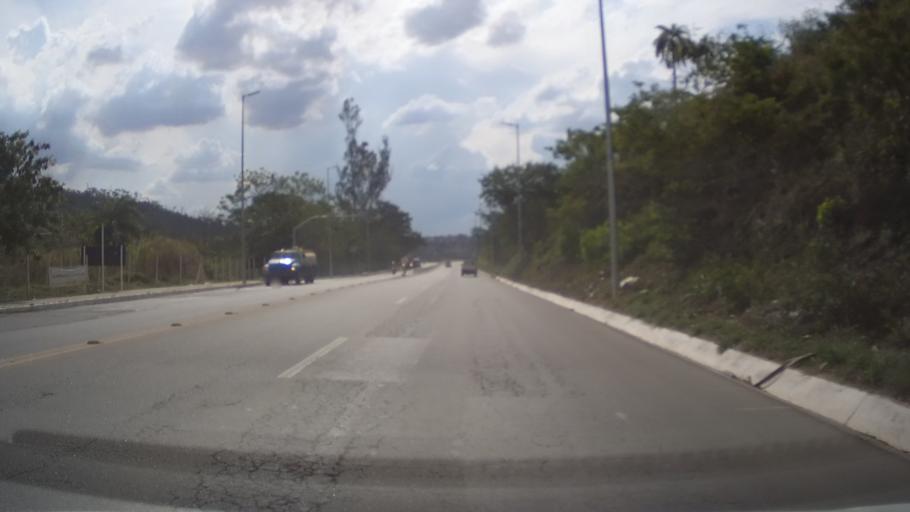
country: BR
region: Minas Gerais
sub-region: Belo Horizonte
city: Belo Horizonte
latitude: -19.8749
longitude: -43.8759
